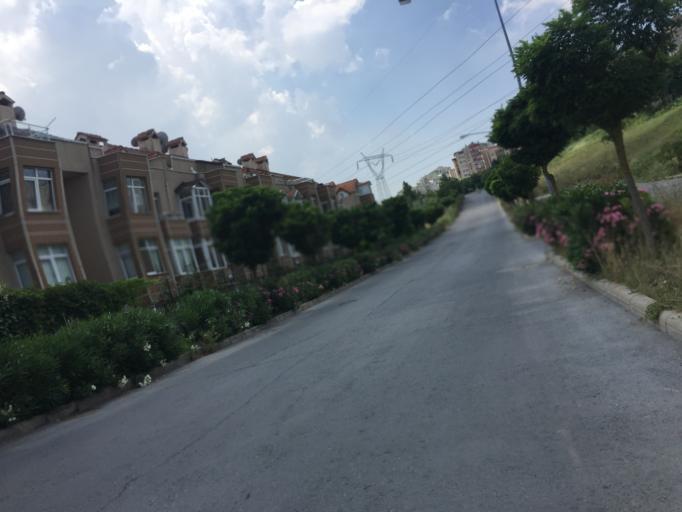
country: TR
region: Istanbul
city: Esenyurt
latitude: 41.0770
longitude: 28.6707
